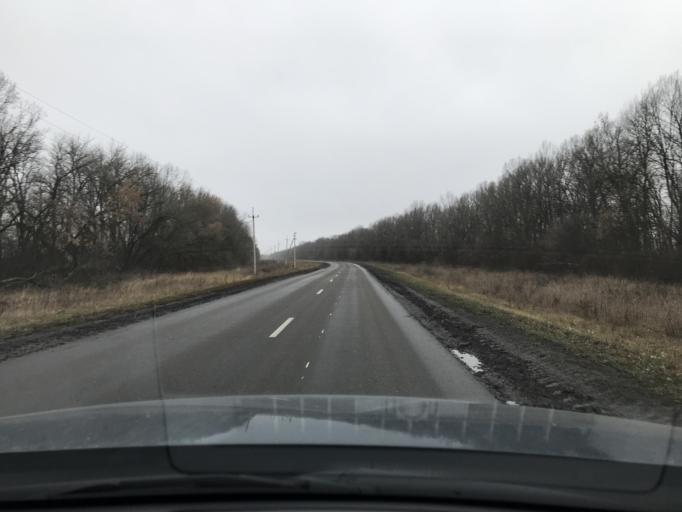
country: RU
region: Penza
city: Zemetchino
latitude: 53.5394
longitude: 42.6650
